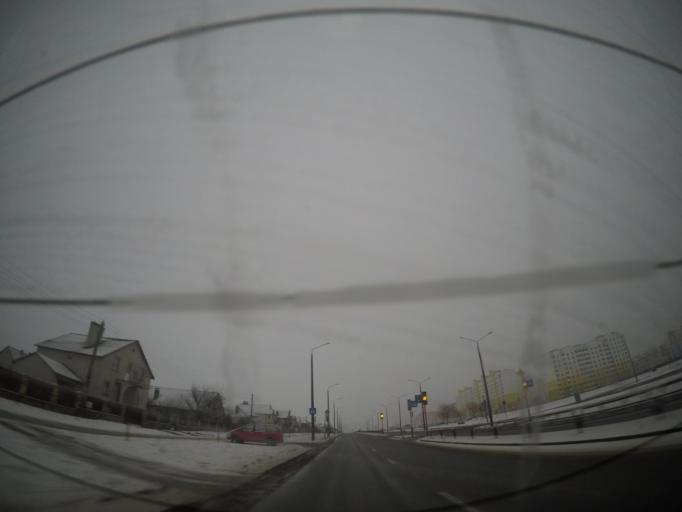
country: BY
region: Grodnenskaya
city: Hrodna
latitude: 53.6259
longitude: 23.8077
